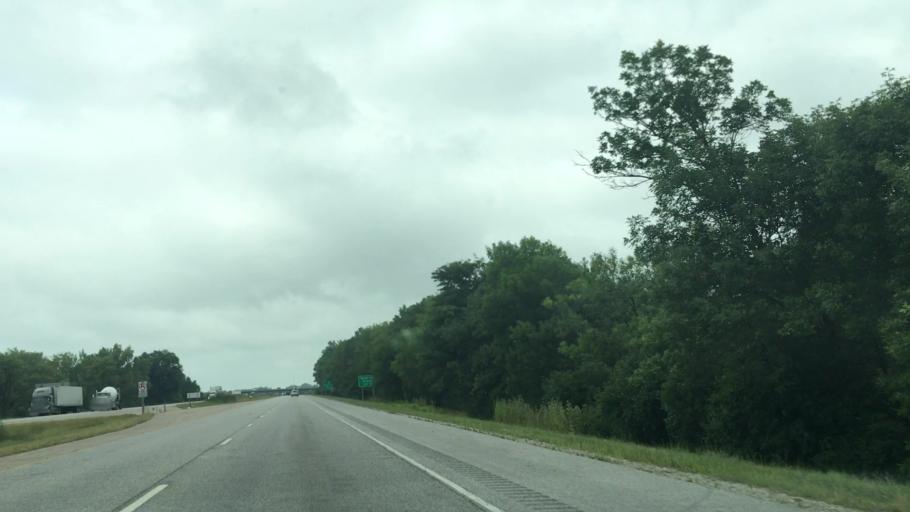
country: US
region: Illinois
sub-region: Rock Island County
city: Milan
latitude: 41.4565
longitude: -90.5266
